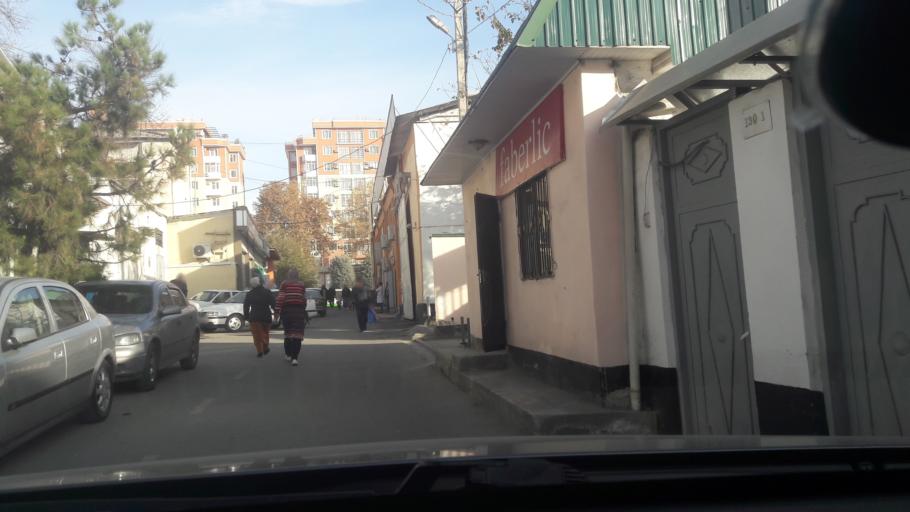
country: TJ
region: Dushanbe
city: Dushanbe
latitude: 38.5832
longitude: 68.7598
